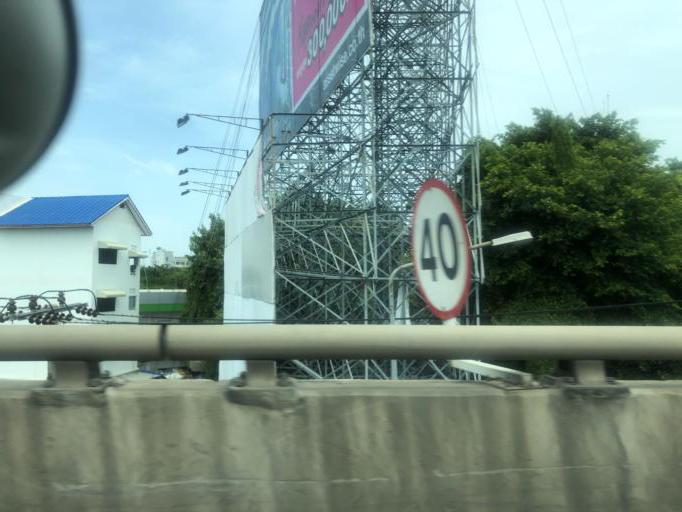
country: TH
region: Bangkok
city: Lak Si
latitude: 13.8738
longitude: 100.5975
